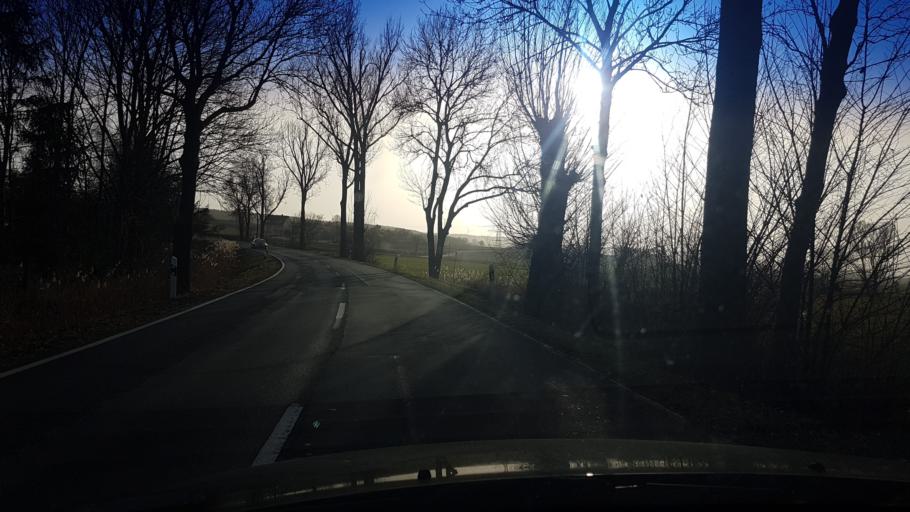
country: DE
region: Bavaria
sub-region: Upper Franconia
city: Pommersfelden
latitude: 49.7552
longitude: 10.8125
